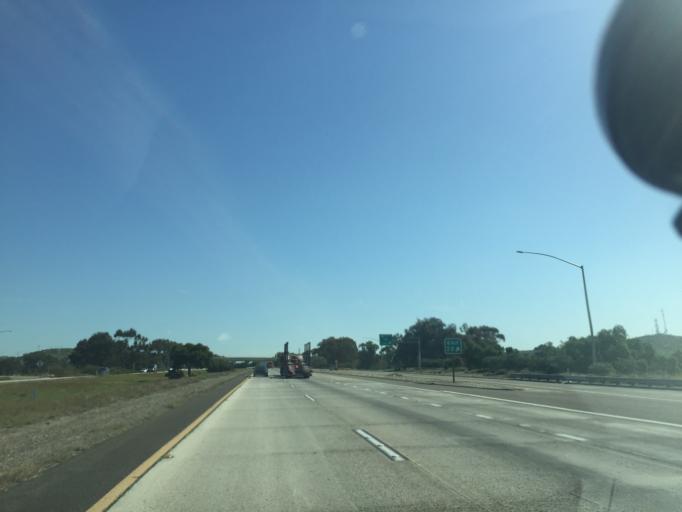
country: US
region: California
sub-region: San Diego County
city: Imperial Beach
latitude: 32.5681
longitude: -117.0455
